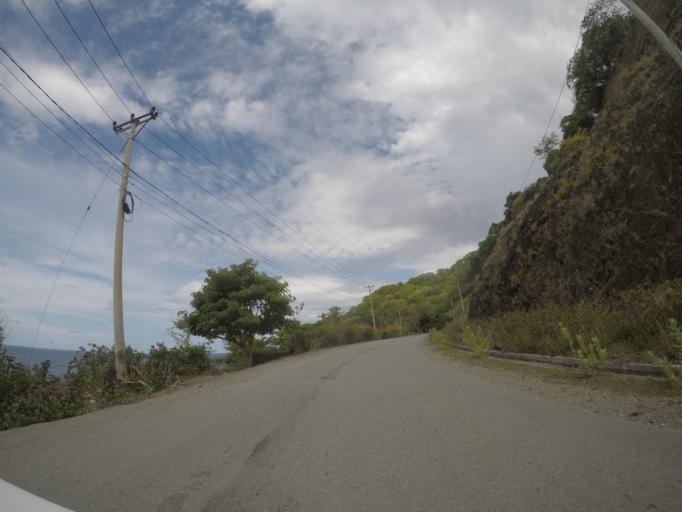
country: TL
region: Liquica
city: Maubara
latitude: -8.6308
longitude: 125.1515
